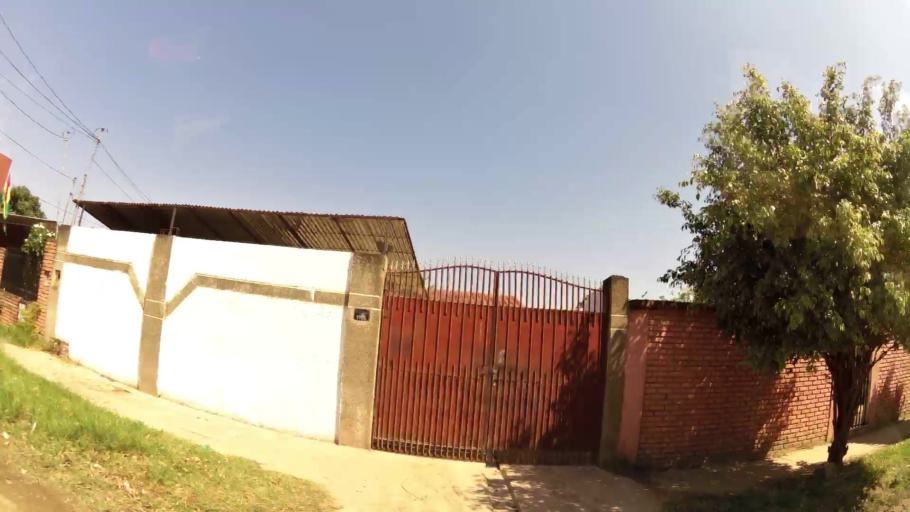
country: BO
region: Santa Cruz
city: Santa Cruz de la Sierra
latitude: -17.7353
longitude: -63.1462
